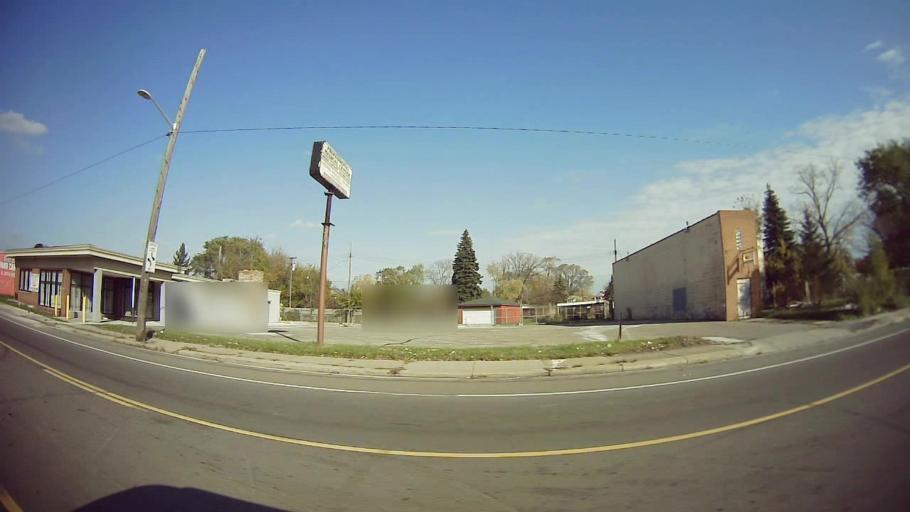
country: US
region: Michigan
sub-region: Wayne County
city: Highland Park
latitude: 42.4263
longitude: -83.0689
